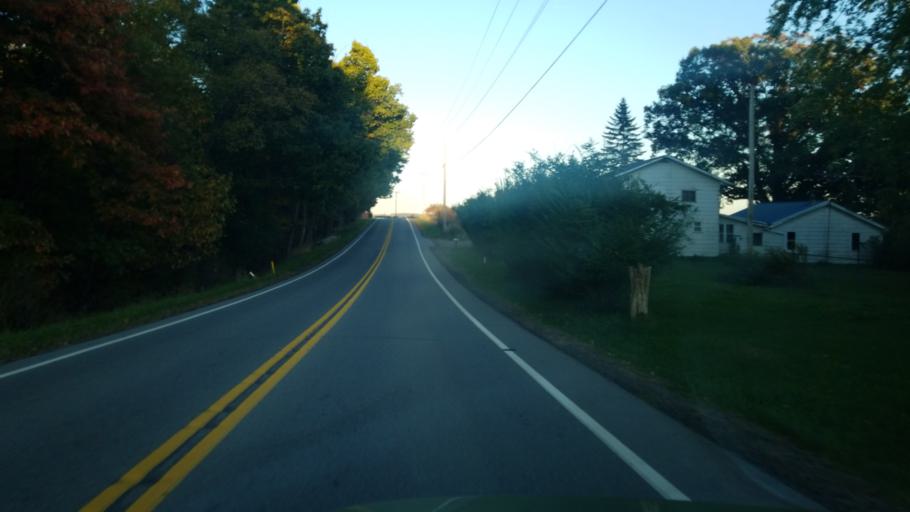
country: US
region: Pennsylvania
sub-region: Jefferson County
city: Reynoldsville
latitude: 41.0645
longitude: -78.9218
